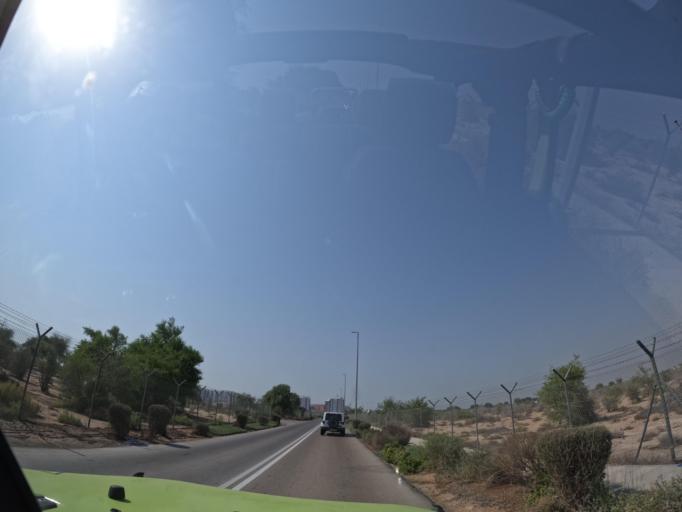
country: AE
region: Abu Dhabi
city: Abu Dhabi
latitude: 24.4774
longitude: 54.6265
